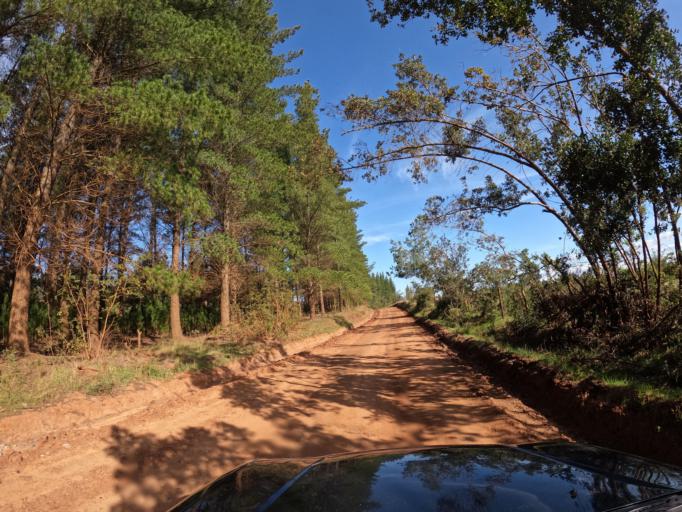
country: CL
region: Biobio
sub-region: Provincia de Biobio
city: La Laja
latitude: -37.1064
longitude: -72.7418
